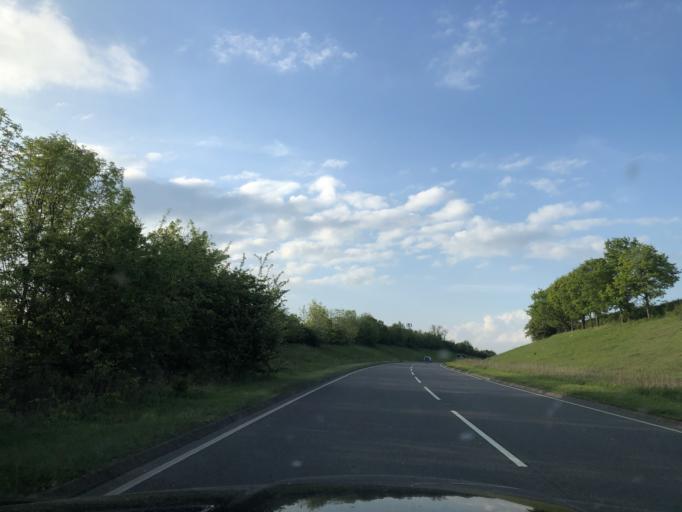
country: GB
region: England
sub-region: Warwickshire
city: Wellesbourne Mountford
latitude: 52.1375
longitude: -1.6153
